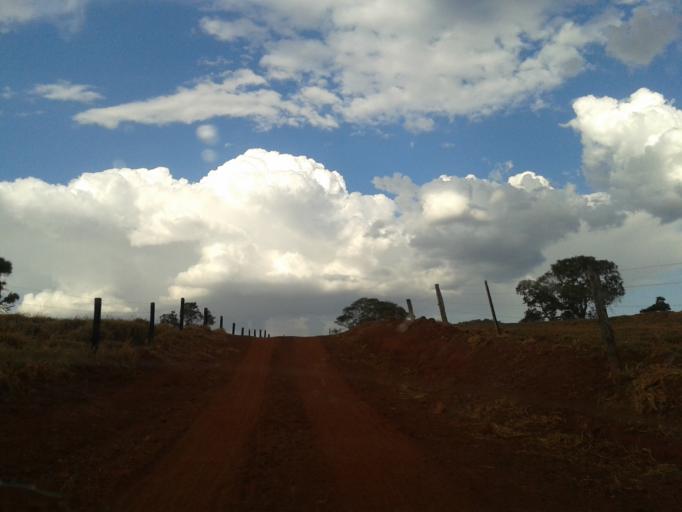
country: BR
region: Minas Gerais
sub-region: Santa Vitoria
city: Santa Vitoria
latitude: -19.1711
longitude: -49.9642
